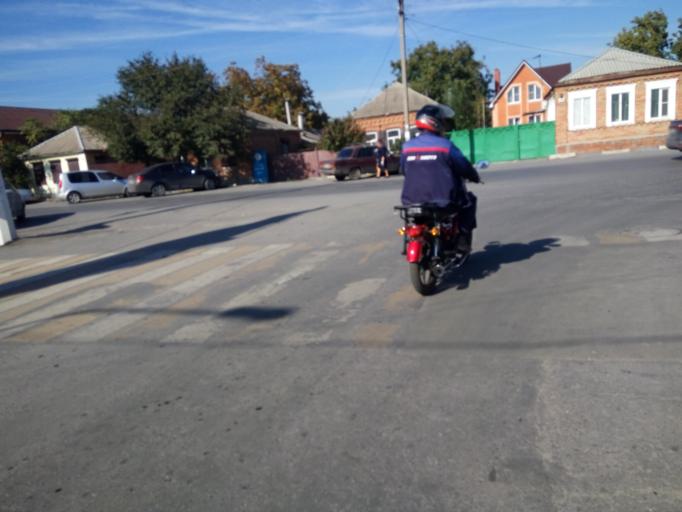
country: RU
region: Rostov
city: Bataysk
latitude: 47.1400
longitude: 39.7356
